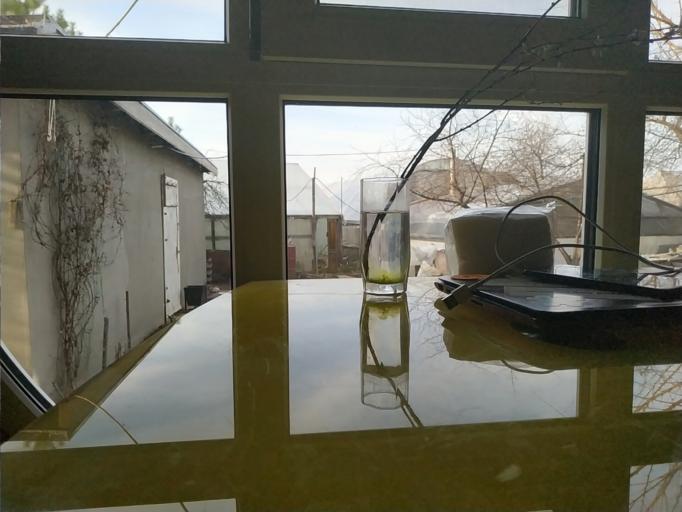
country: RU
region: Republic of Karelia
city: Suoyarvi
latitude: 61.7631
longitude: 32.3179
